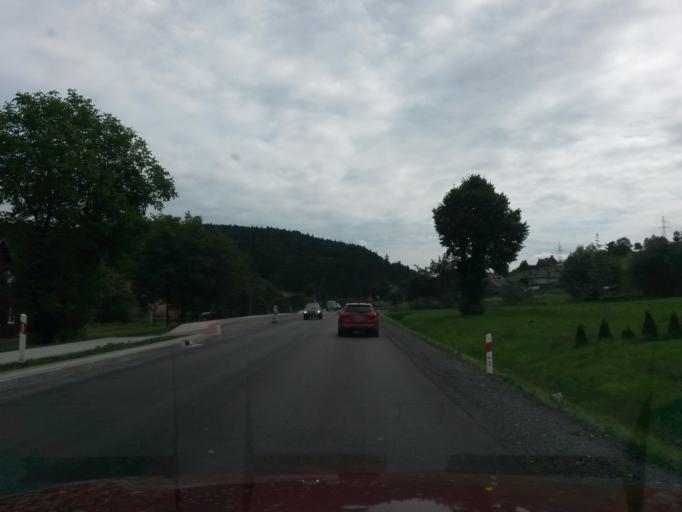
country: PL
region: Lesser Poland Voivodeship
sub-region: Powiat nowosadecki
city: Labowa
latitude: 49.4908
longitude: 20.9098
